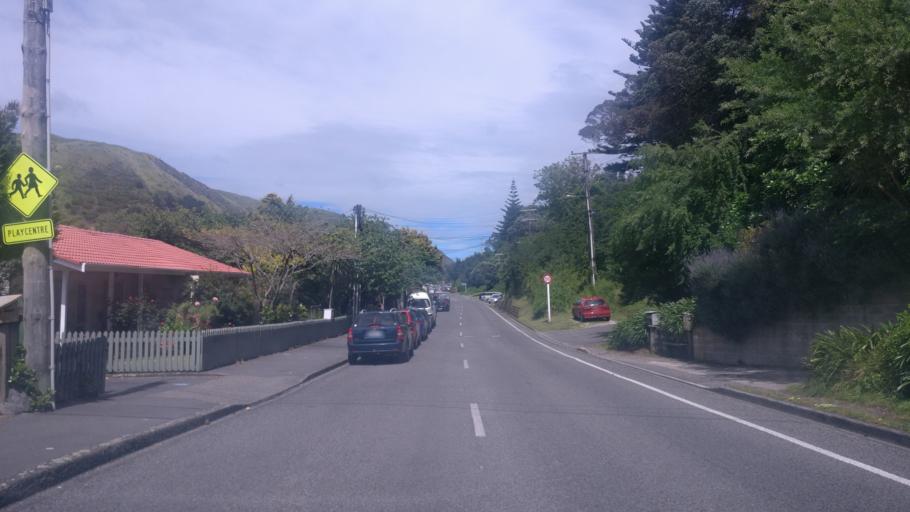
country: NZ
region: Wellington
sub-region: Kapiti Coast District
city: Paraparaumu
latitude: -40.9855
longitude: 174.9538
